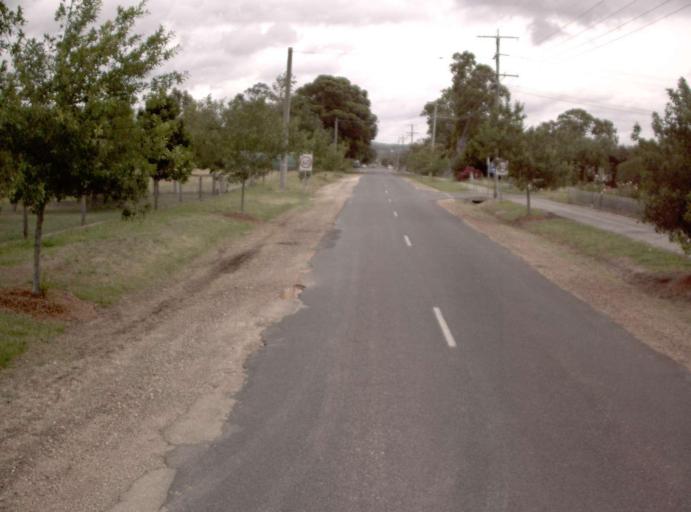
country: AU
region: Victoria
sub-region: Wellington
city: Sale
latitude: -37.8467
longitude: 147.0720
